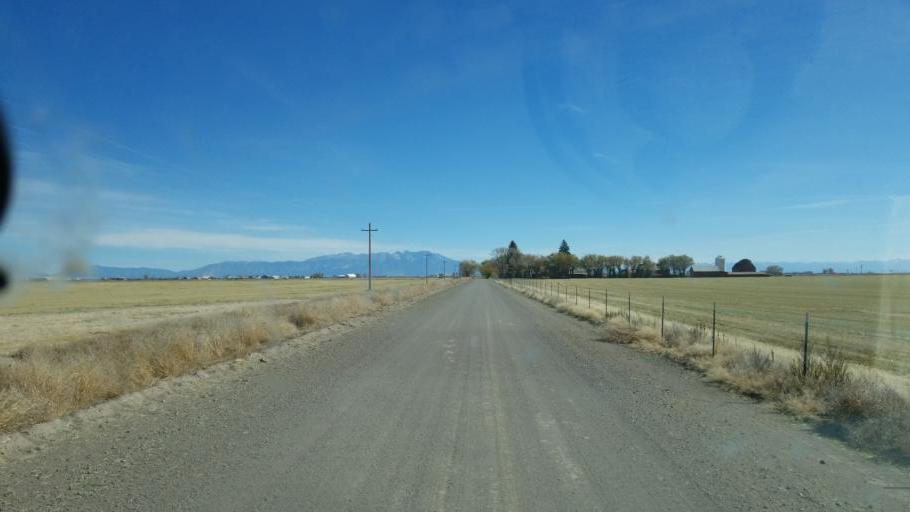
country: US
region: Colorado
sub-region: Rio Grande County
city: Monte Vista
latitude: 37.5313
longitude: -106.0648
